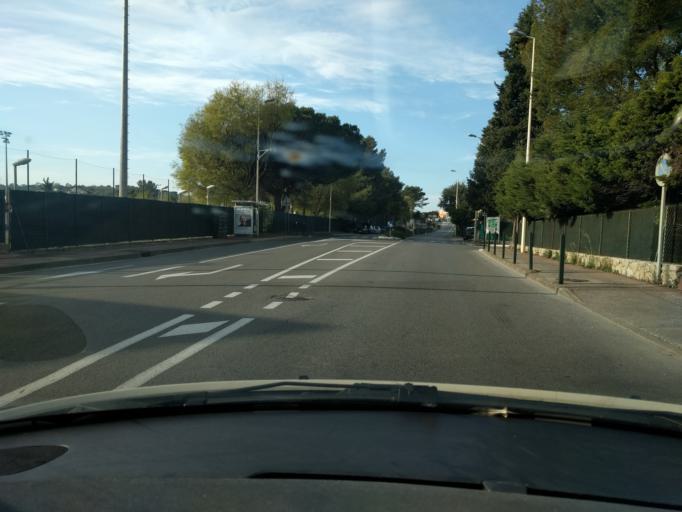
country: FR
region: Provence-Alpes-Cote d'Azur
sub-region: Departement des Alpes-Maritimes
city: Mougins
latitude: 43.5709
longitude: 6.9825
